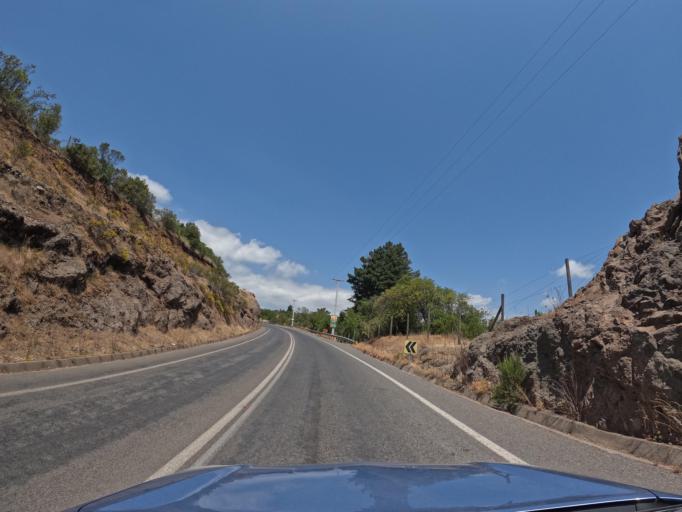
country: CL
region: Maule
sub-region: Provincia de Curico
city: Molina
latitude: -35.1810
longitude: -71.1176
